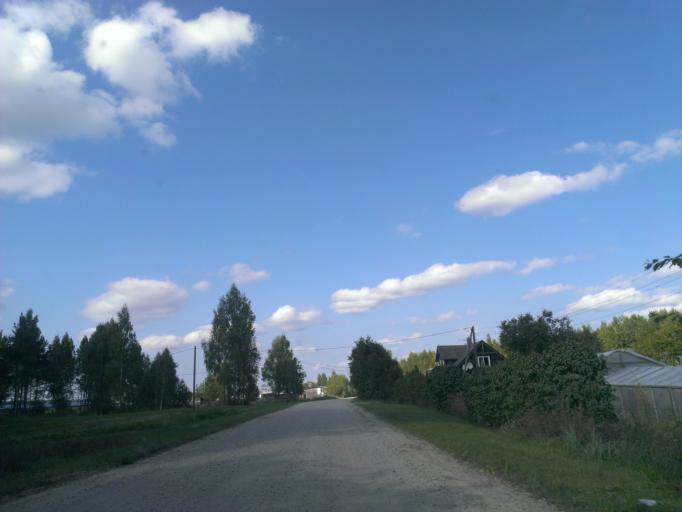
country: LV
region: Incukalns
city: Vangazi
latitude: 57.1012
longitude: 24.5639
